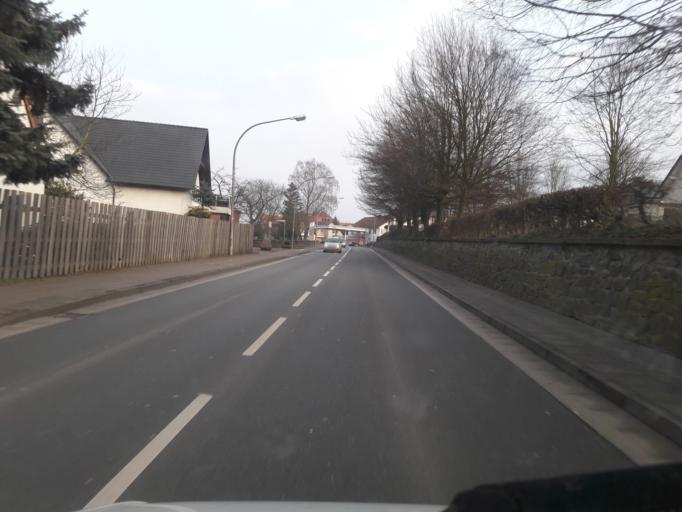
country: DE
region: North Rhine-Westphalia
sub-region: Regierungsbezirk Detmold
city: Huellhorst
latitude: 52.3027
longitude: 8.6940
